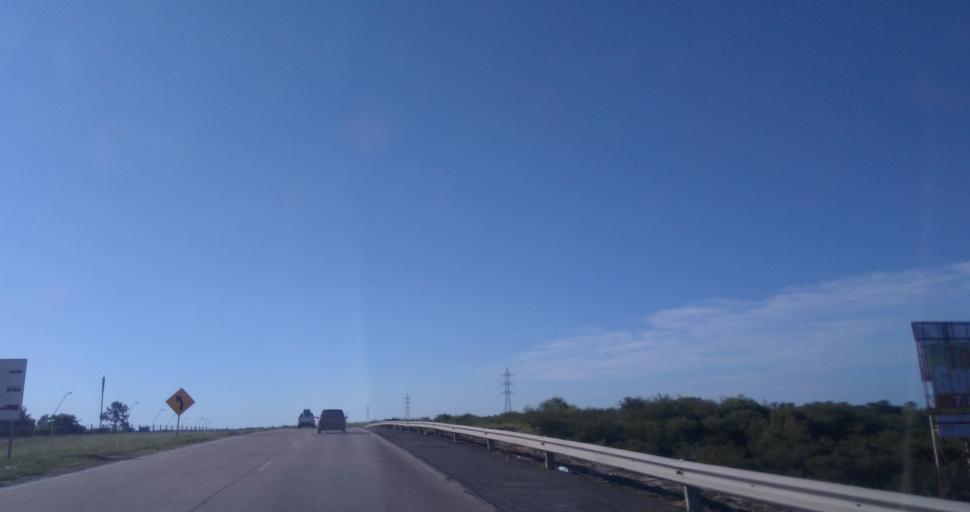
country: AR
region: Chaco
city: Barranqueras
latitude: -27.4414
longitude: -58.8925
